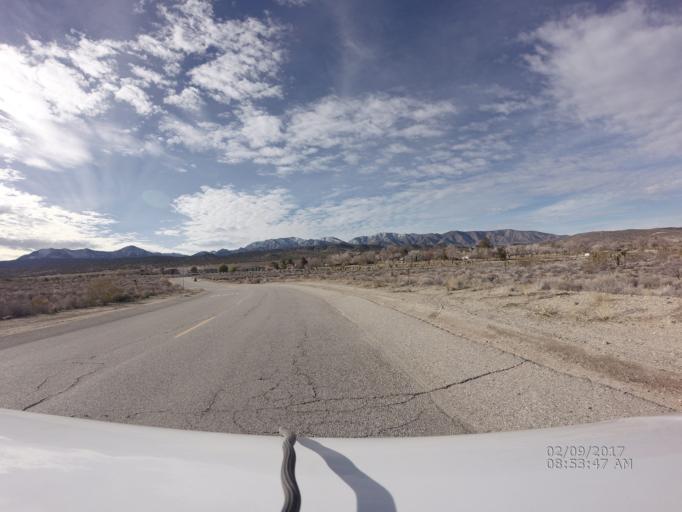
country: US
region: California
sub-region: Los Angeles County
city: Lake Los Angeles
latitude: 34.4772
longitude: -117.8370
